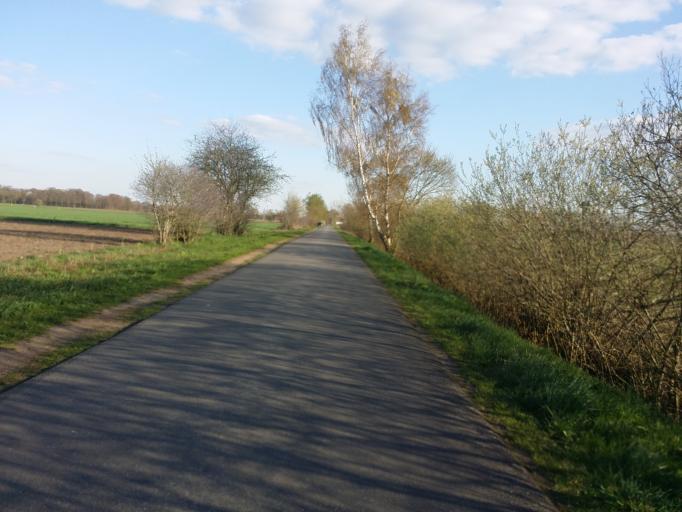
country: DE
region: Lower Saxony
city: Delmenhorst
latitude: 53.0124
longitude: 8.6302
